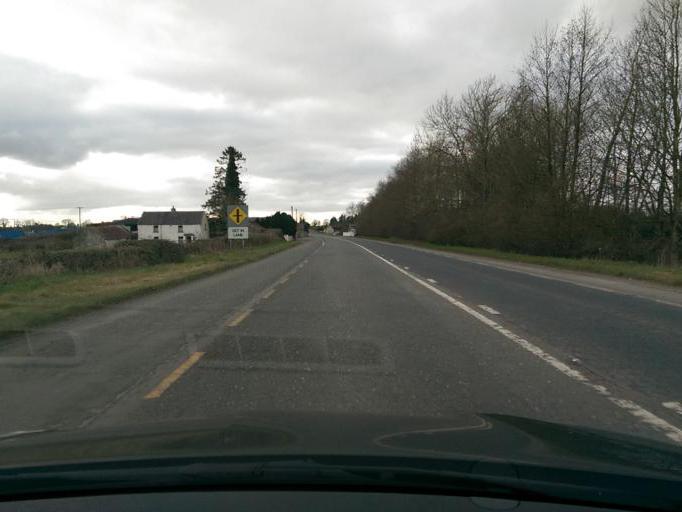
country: IE
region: Leinster
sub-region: An Iarmhi
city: Moate
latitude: 53.3923
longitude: -7.8152
